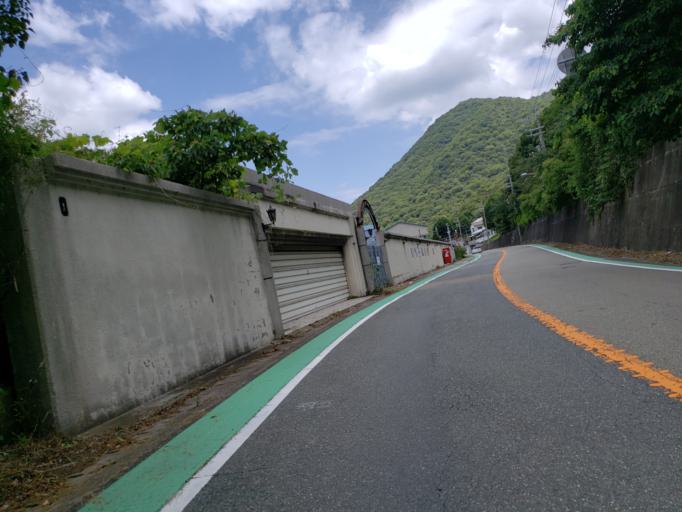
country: JP
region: Hyogo
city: Aioi
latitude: 34.7723
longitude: 134.4706
